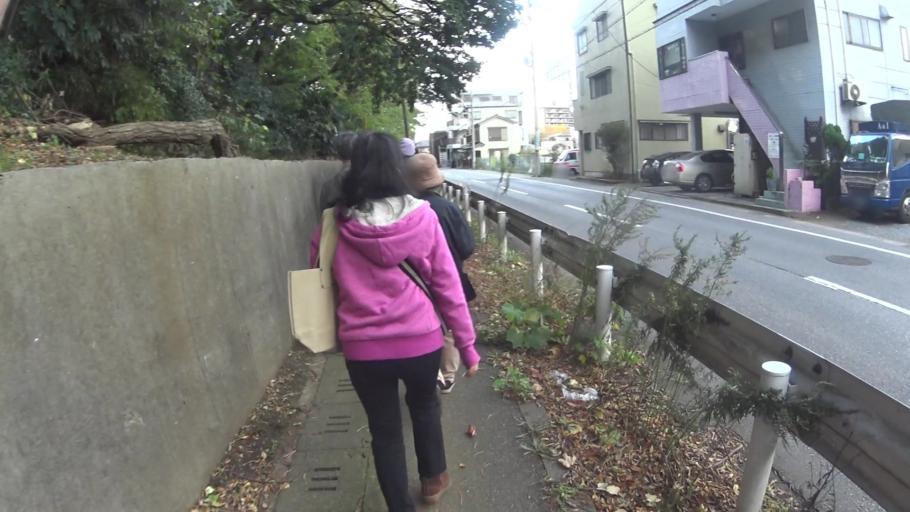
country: JP
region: Chiba
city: Chiba
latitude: 35.6061
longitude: 140.1298
